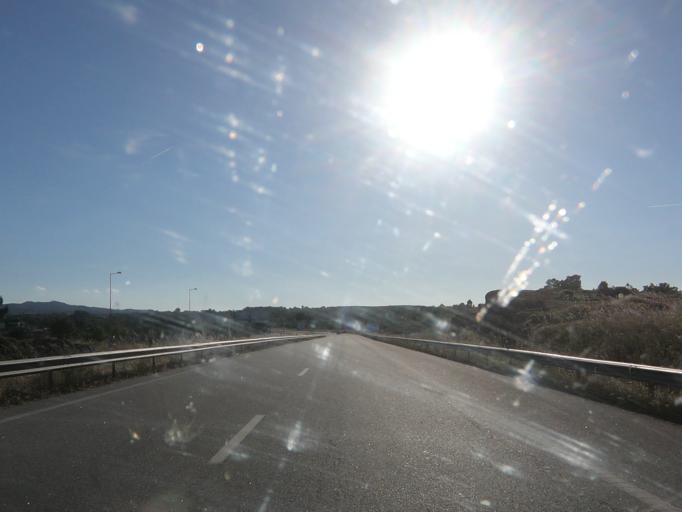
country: PT
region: Guarda
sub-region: Guarda
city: Sequeira
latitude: 40.6054
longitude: -7.0707
